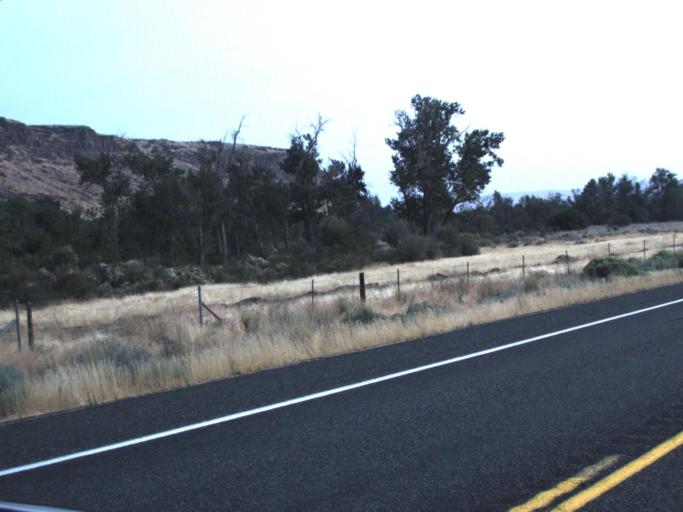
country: US
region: Washington
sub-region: Yakima County
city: Toppenish
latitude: 46.2194
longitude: -120.4367
